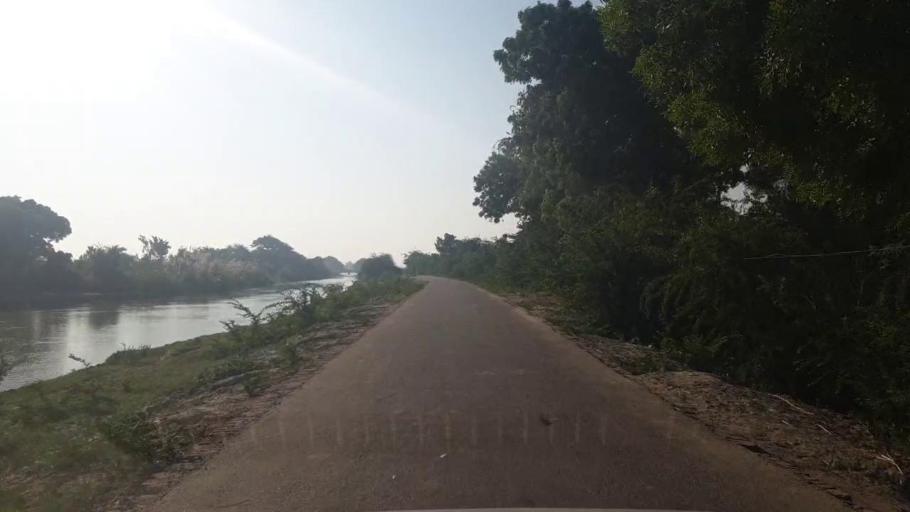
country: PK
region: Sindh
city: Tando Bago
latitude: 24.7252
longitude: 68.9381
